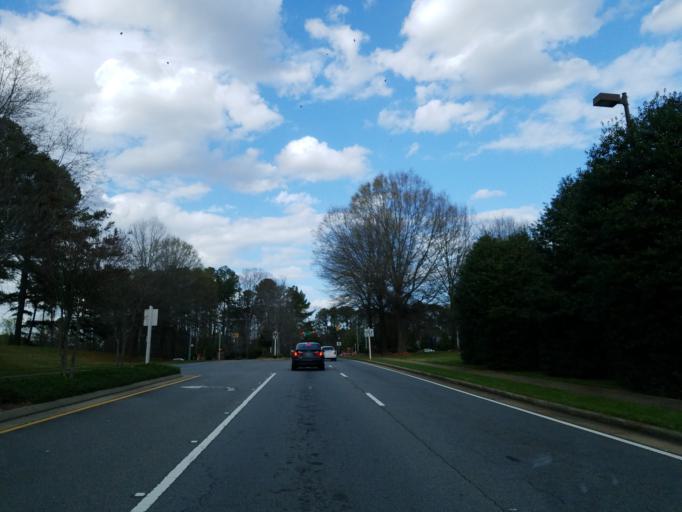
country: US
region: Georgia
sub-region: Cobb County
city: Kennesaw
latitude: 34.0343
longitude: -84.5552
